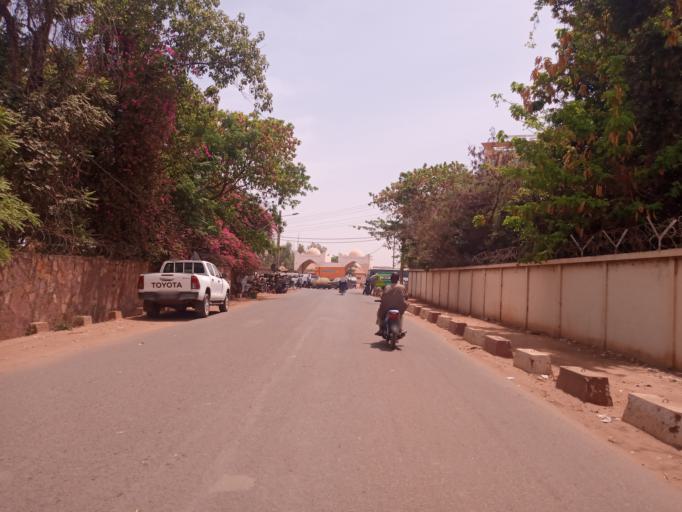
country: ML
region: Bamako
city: Bamako
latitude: 12.6359
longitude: -7.9934
